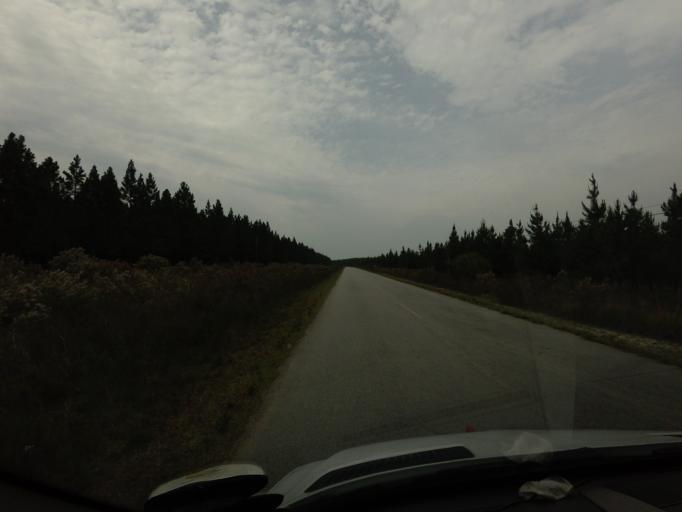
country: ZA
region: Eastern Cape
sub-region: Cacadu District Municipality
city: Kareedouw
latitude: -33.9742
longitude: 23.8401
